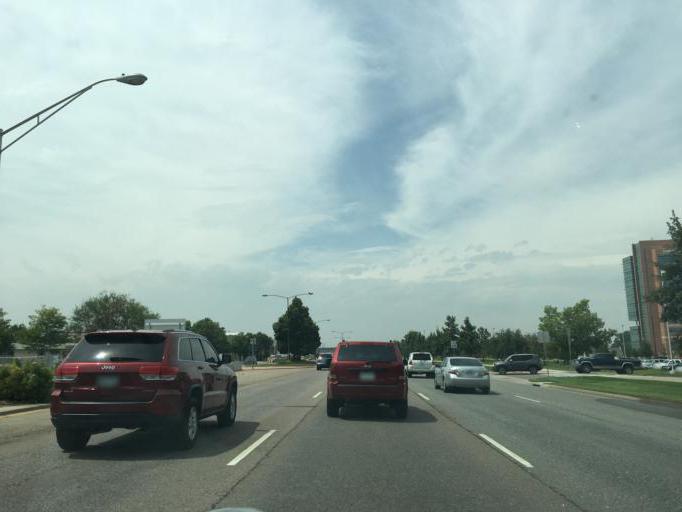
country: US
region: Colorado
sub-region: Adams County
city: Aurora
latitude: 39.7403
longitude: -104.8389
